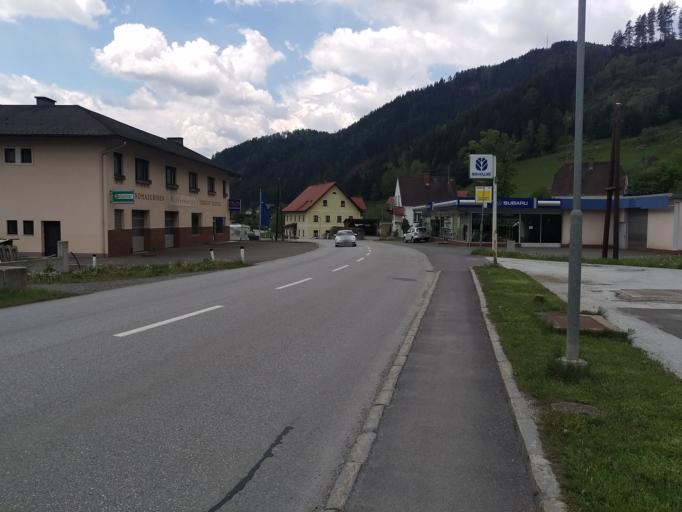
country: AT
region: Styria
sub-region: Politischer Bezirk Bruck-Muerzzuschlag
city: Allerheiligen im Muerztal
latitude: 47.3906
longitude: 15.4263
